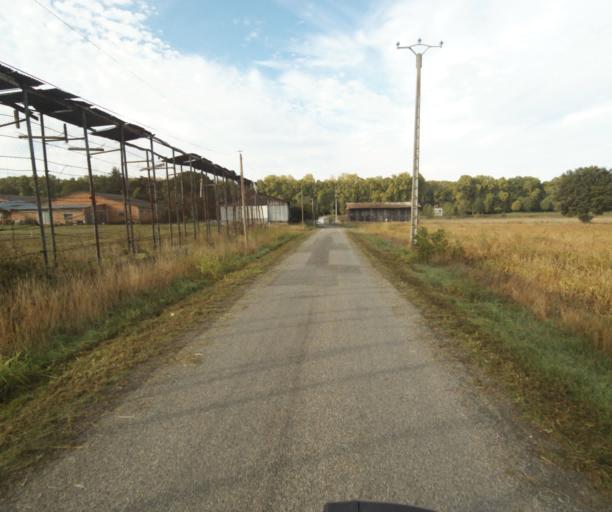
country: FR
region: Midi-Pyrenees
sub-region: Departement du Tarn-et-Garonne
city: Montech
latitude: 43.9750
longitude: 1.2261
